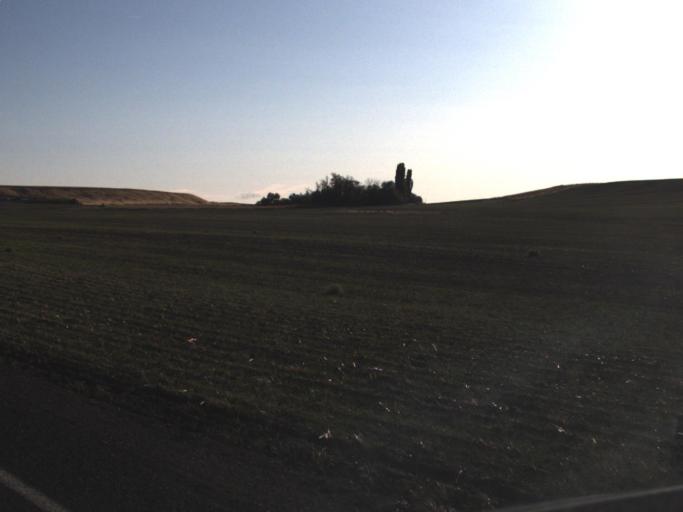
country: US
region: Washington
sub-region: Adams County
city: Ritzville
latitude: 46.8478
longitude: -118.3339
